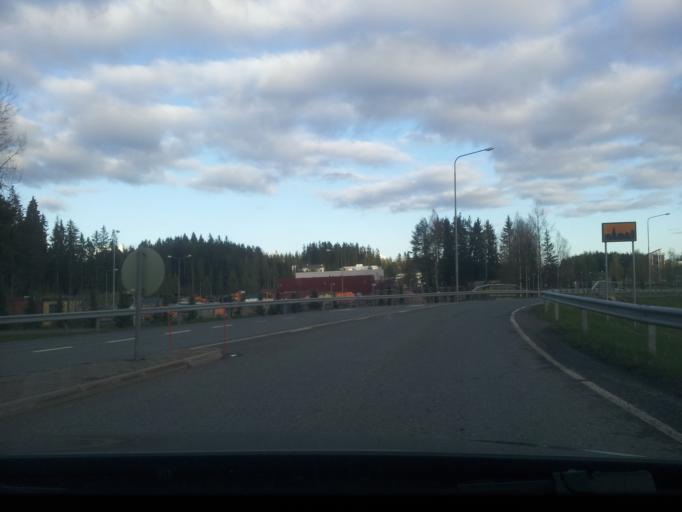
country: FI
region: Haeme
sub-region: Riihimaeki
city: Riihimaeki
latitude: 60.7516
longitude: 24.7421
